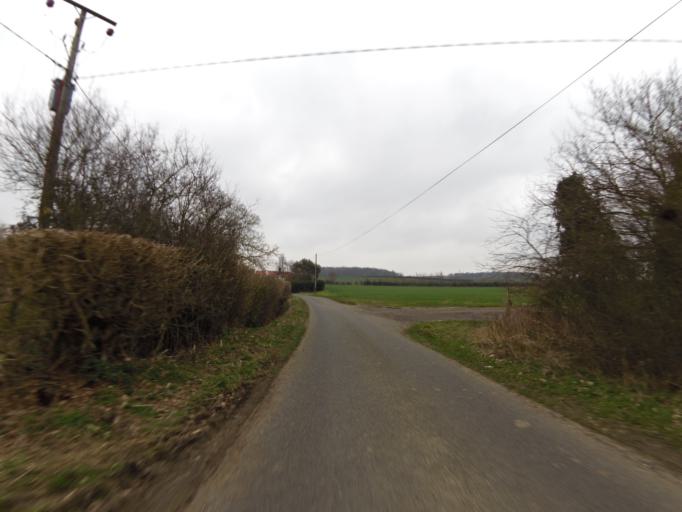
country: GB
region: England
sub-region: Suffolk
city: Framlingham
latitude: 52.2086
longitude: 1.3296
